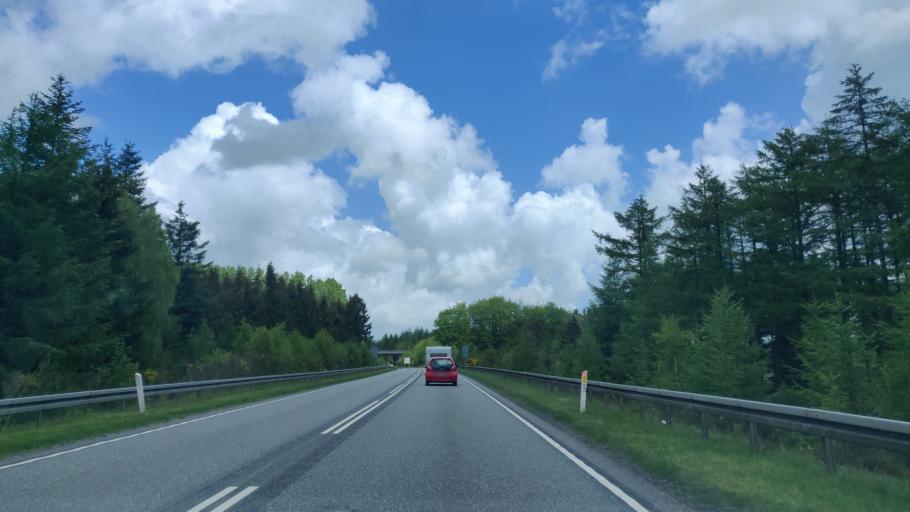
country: DK
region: Central Jutland
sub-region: Hedensted Kommune
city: Torring
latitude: 55.9583
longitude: 9.4015
